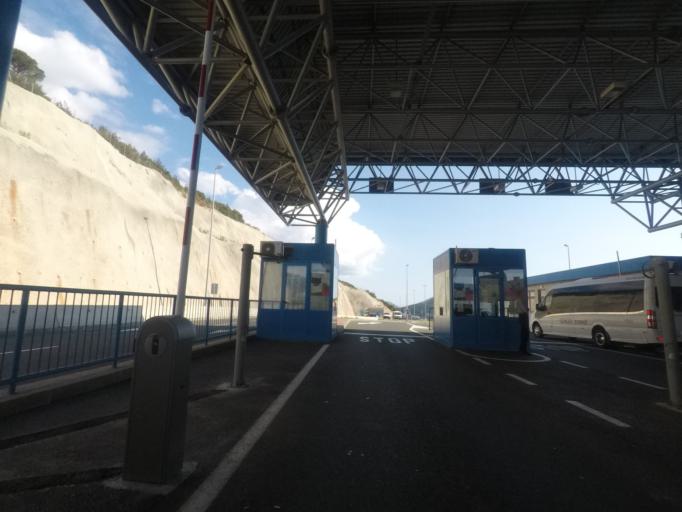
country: BA
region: Federation of Bosnia and Herzegovina
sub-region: Hercegovacko-Bosanski Kanton
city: Neum
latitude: 42.8886
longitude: 17.6527
